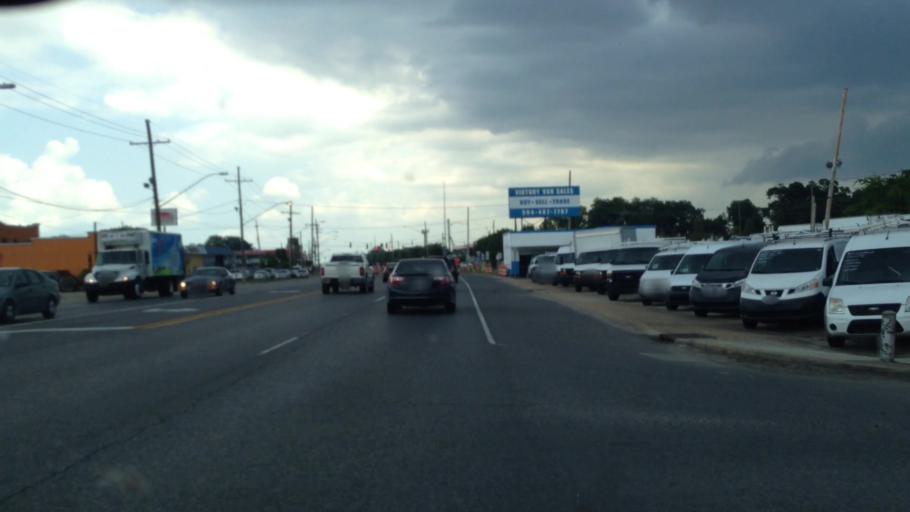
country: US
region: Louisiana
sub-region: Jefferson Parish
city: Kenner
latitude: 29.9801
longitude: -90.2471
